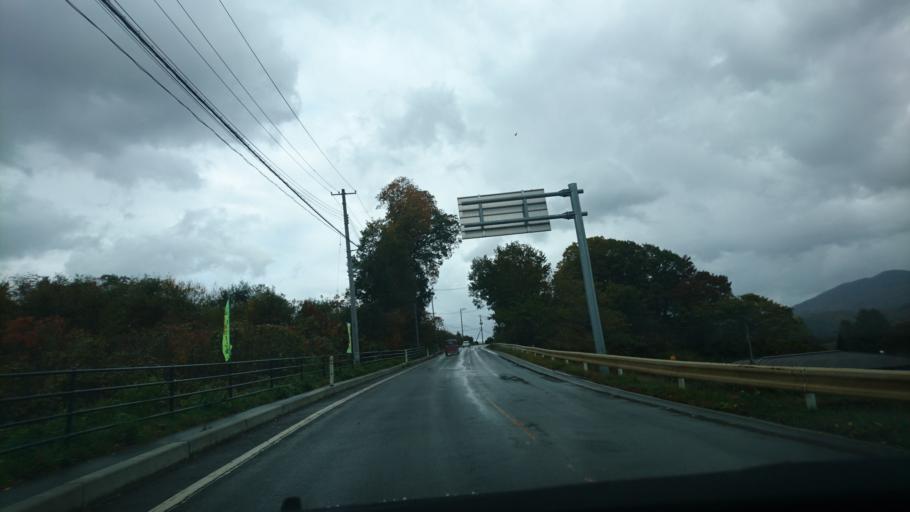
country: JP
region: Iwate
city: Shizukuishi
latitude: 39.6681
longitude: 140.9704
